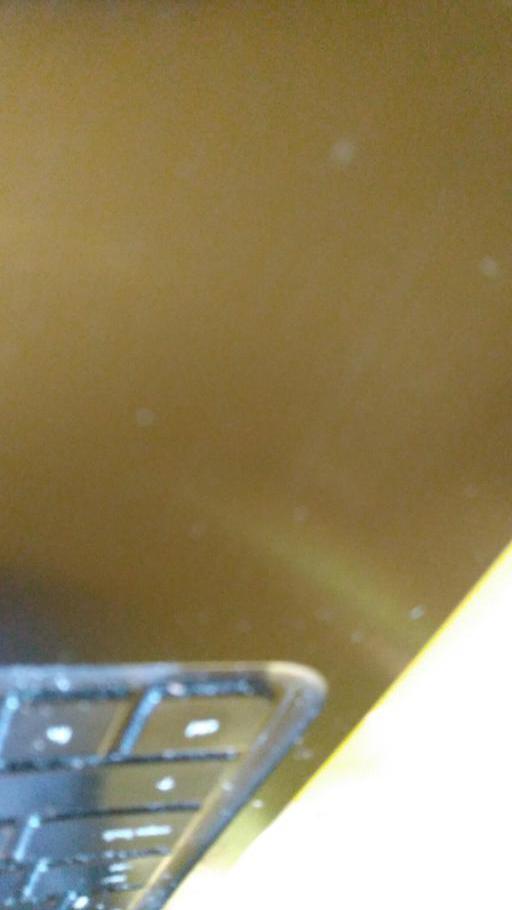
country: RU
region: Moskovskaya
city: Troitskoye
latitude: 55.2387
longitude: 38.5824
